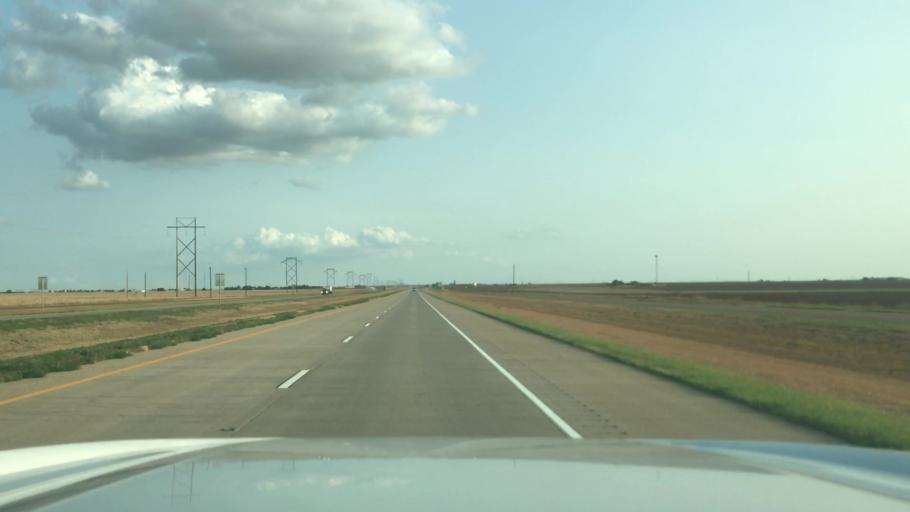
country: US
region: Texas
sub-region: Swisher County
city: Tulia
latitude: 34.5573
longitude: -101.7950
